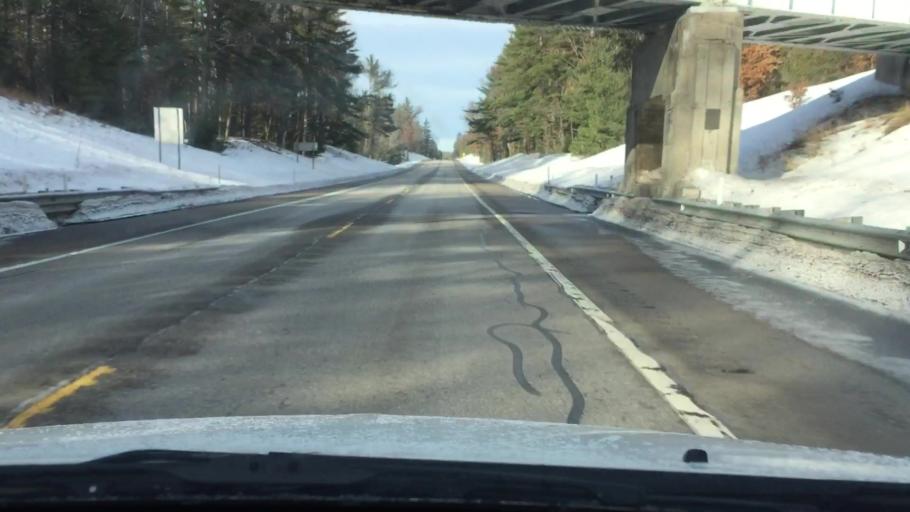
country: US
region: Michigan
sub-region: Wexford County
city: Manton
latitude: 44.5641
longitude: -85.3667
